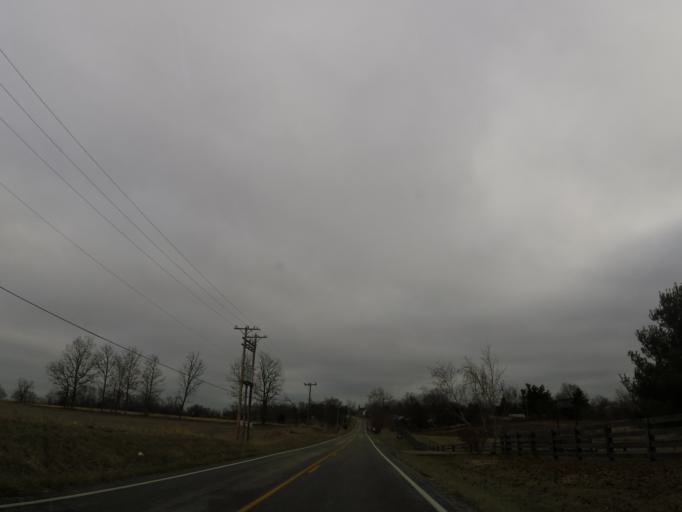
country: US
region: Kentucky
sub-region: Henry County
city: Eminence
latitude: 38.3609
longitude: -85.1172
